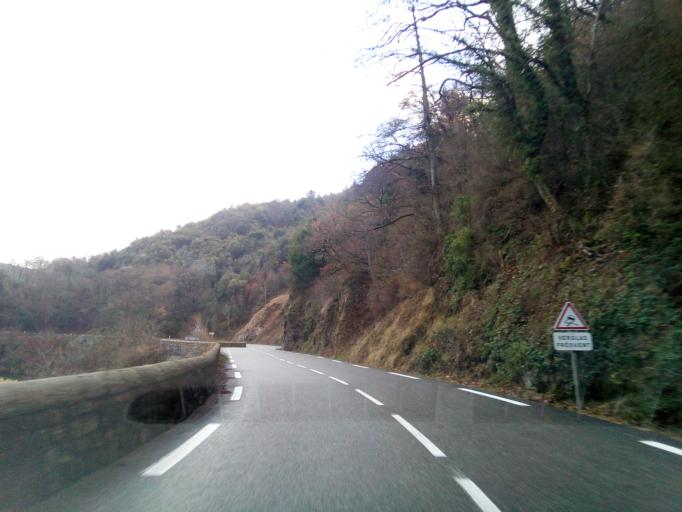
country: FR
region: Rhone-Alpes
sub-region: Departement de l'Ardeche
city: Saint-Sauveur-de-Montagut
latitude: 44.8734
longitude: 4.5391
